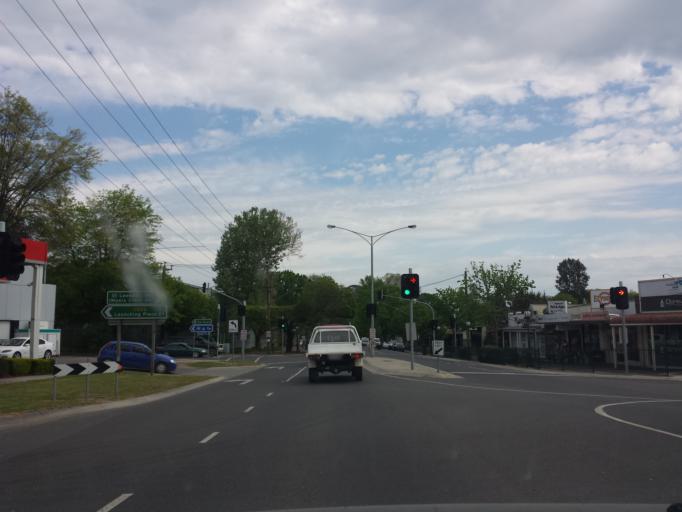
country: AU
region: Victoria
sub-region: Yarra Ranges
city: Healesville
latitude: -37.6503
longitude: 145.5234
